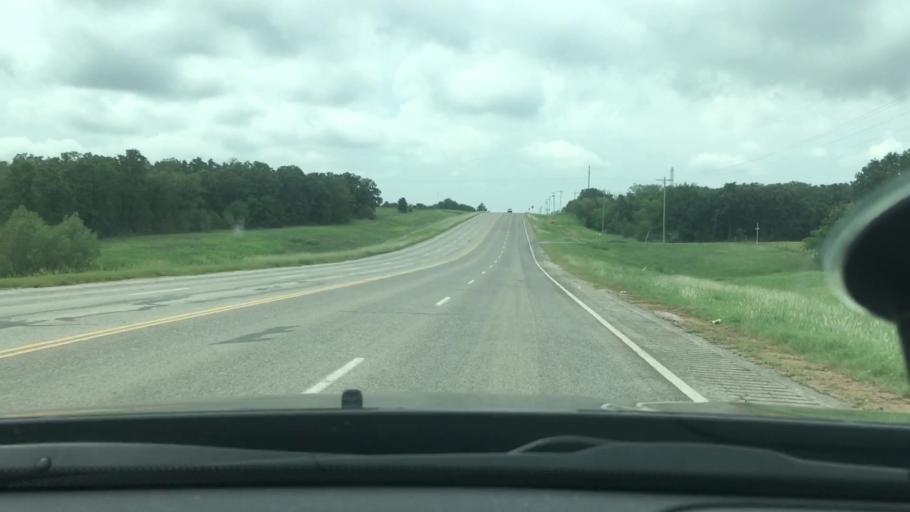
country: US
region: Oklahoma
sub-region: Carter County
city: Healdton
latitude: 34.1833
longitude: -97.4749
